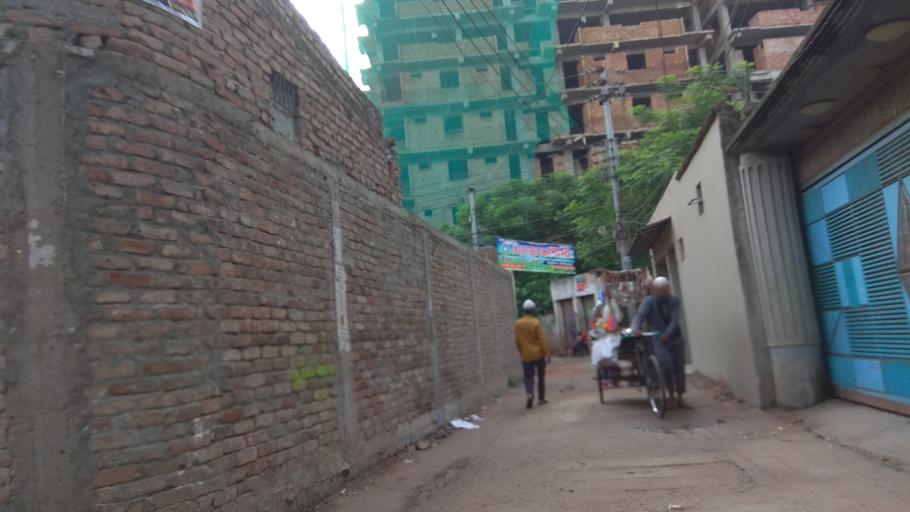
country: BD
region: Dhaka
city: Azimpur
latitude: 23.7929
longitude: 90.3798
